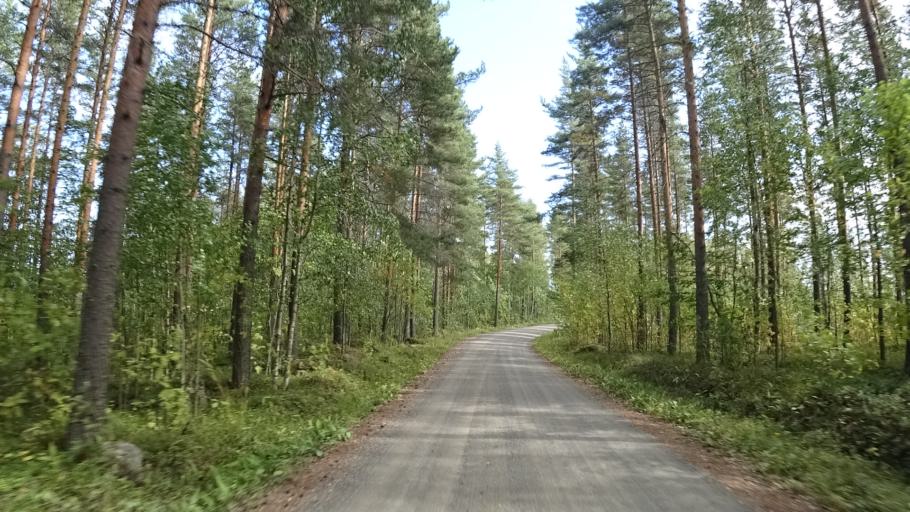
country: FI
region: North Karelia
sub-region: Keski-Karjala
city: Raeaekkylae
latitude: 62.3897
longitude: 29.7802
